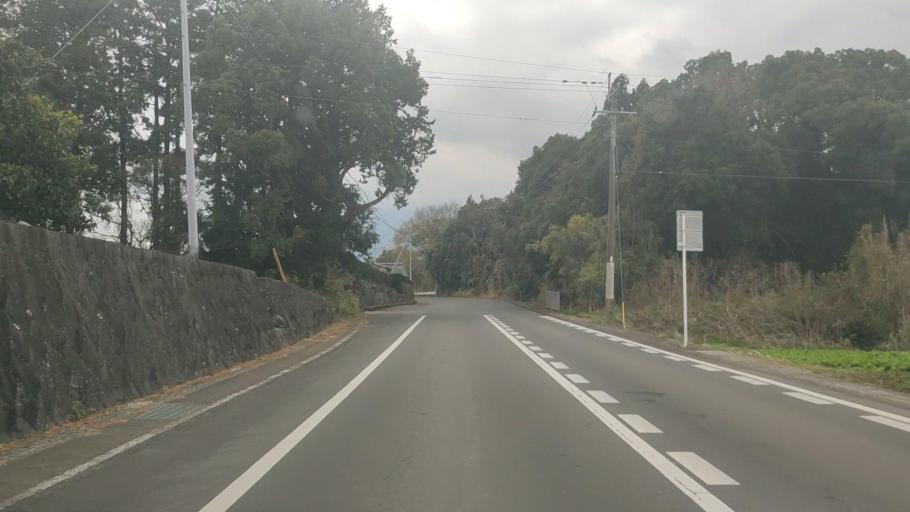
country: JP
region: Nagasaki
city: Shimabara
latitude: 32.8344
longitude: 130.2913
